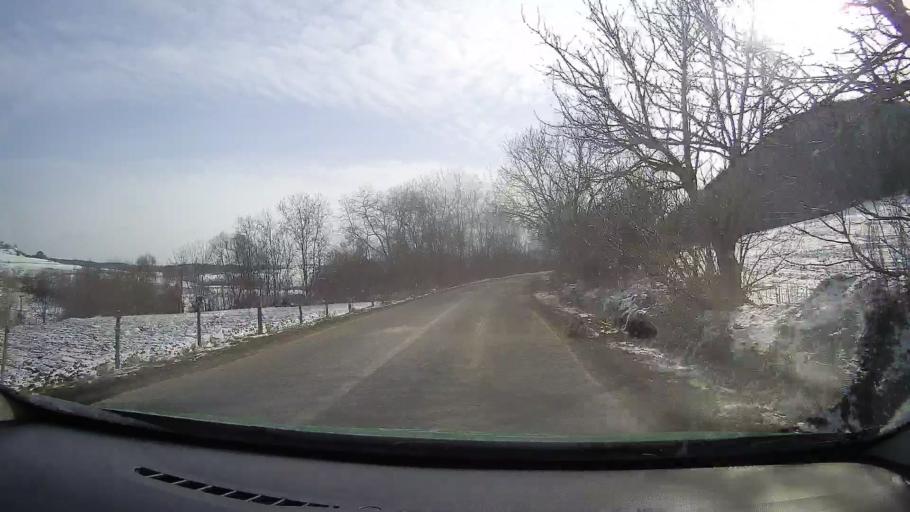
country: RO
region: Mures
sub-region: Comuna Apold
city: Saes
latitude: 46.1927
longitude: 24.7649
